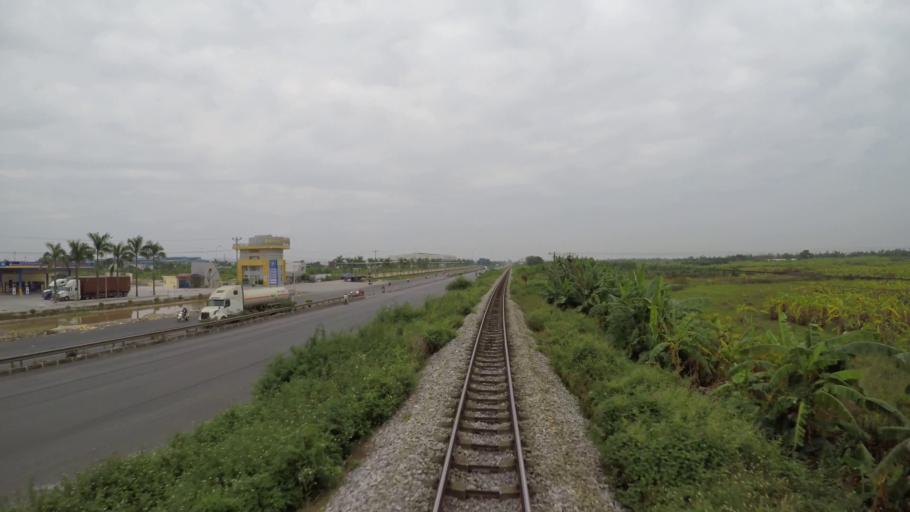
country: VN
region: Hai Duong
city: Nam Sach
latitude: 20.9756
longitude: 106.3968
